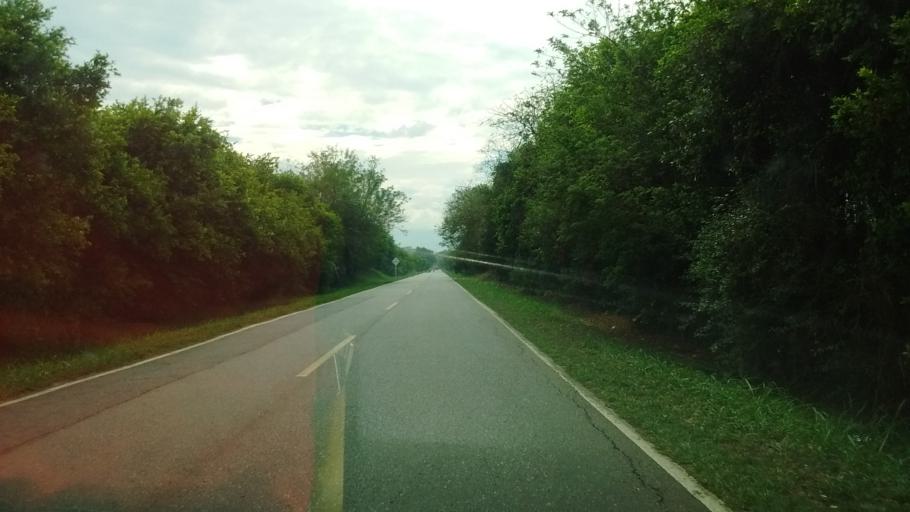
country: CO
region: Cauca
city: Caloto
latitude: 3.0471
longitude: -76.4370
